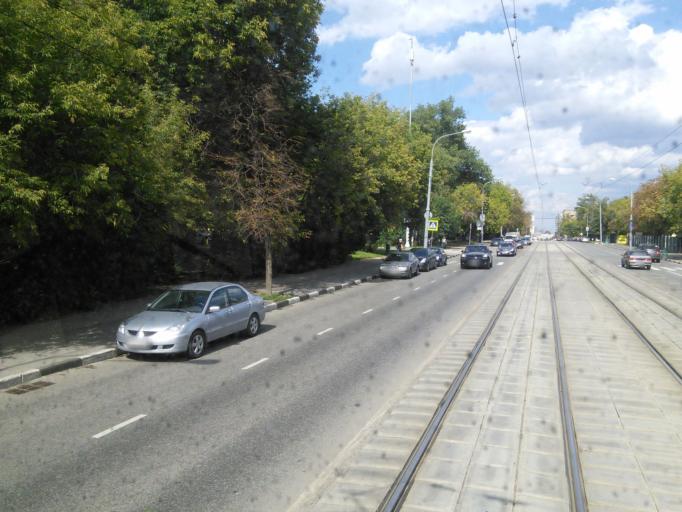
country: RU
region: Moskovskaya
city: Leninskiye Gory
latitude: 55.6991
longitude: 37.5747
